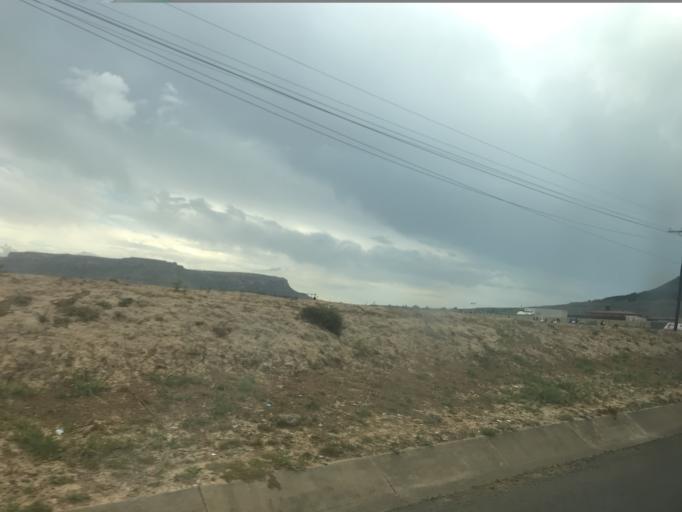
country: LS
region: Maseru
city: Maseru
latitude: -29.3759
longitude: 27.4818
